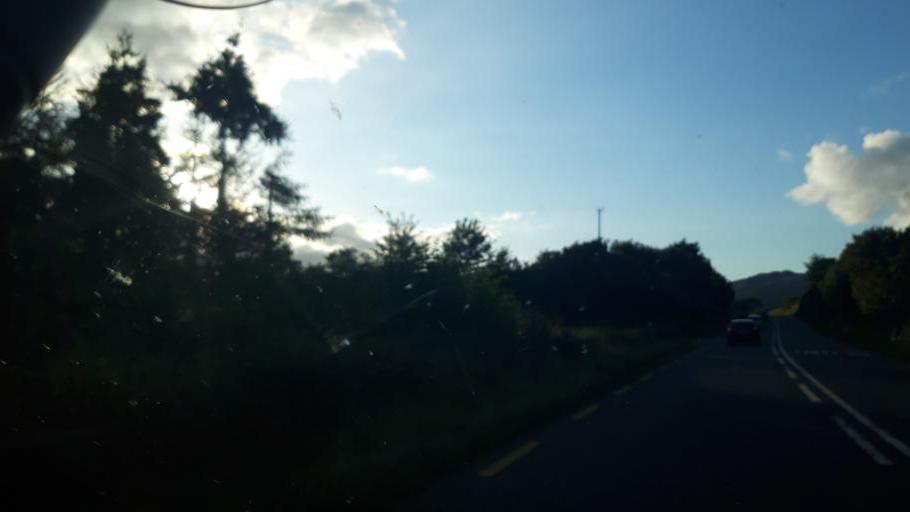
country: IE
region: Leinster
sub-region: Lu
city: Carlingford
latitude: 53.9947
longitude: -6.2235
